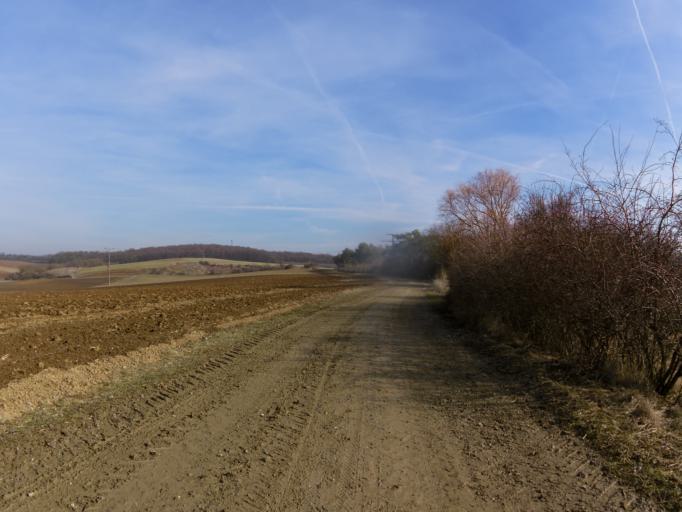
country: DE
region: Bavaria
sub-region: Regierungsbezirk Unterfranken
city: Estenfeld
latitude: 49.8255
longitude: 10.0286
